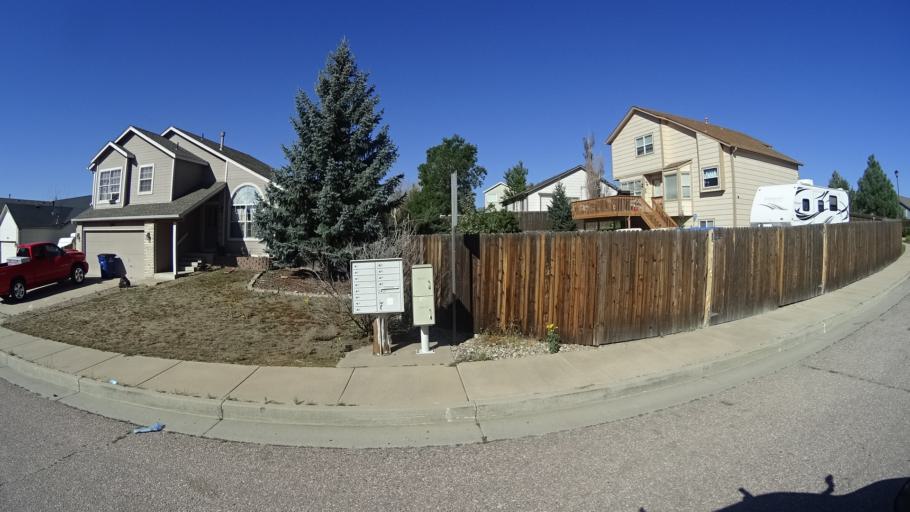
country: US
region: Colorado
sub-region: El Paso County
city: Black Forest
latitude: 38.9465
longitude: -104.7339
